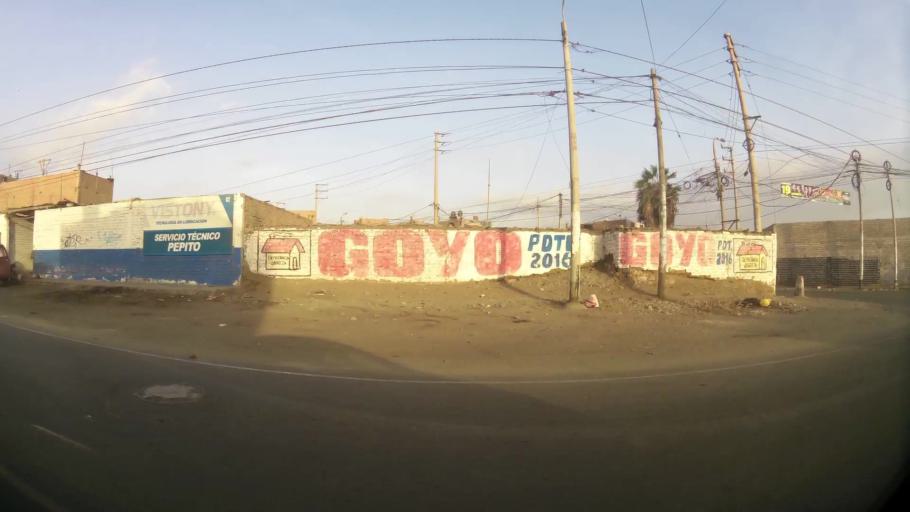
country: PE
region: Lima
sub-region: Huaura
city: Hualmay
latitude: -11.1037
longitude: -77.6143
